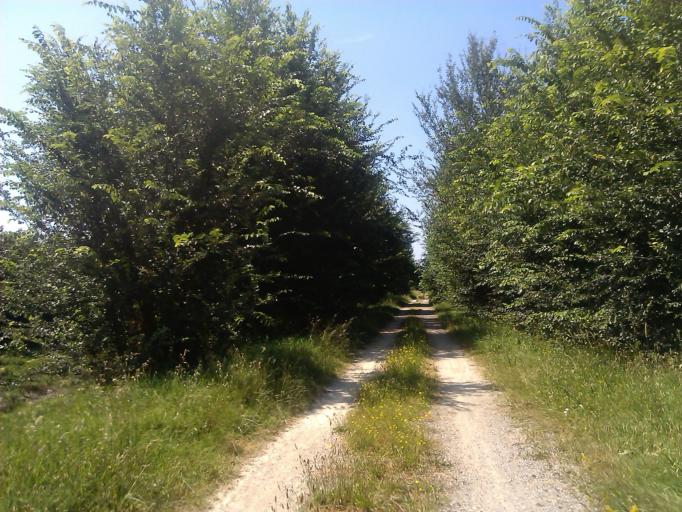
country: IT
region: Tuscany
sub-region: Province of Arezzo
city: Cesa
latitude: 43.3552
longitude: 11.8266
